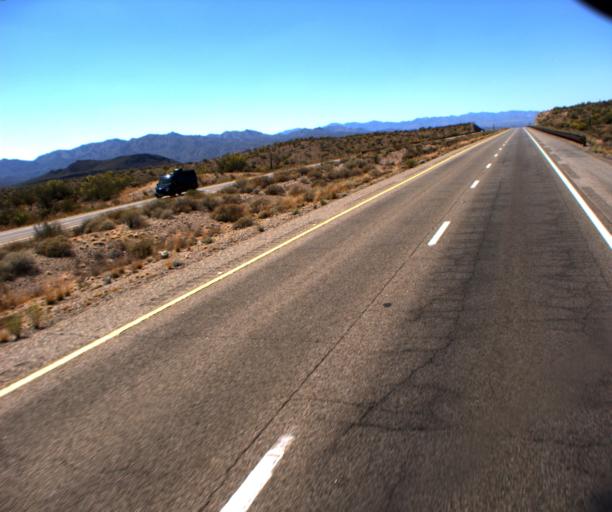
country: US
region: Arizona
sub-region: Yavapai County
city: Bagdad
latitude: 34.5885
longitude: -113.5089
